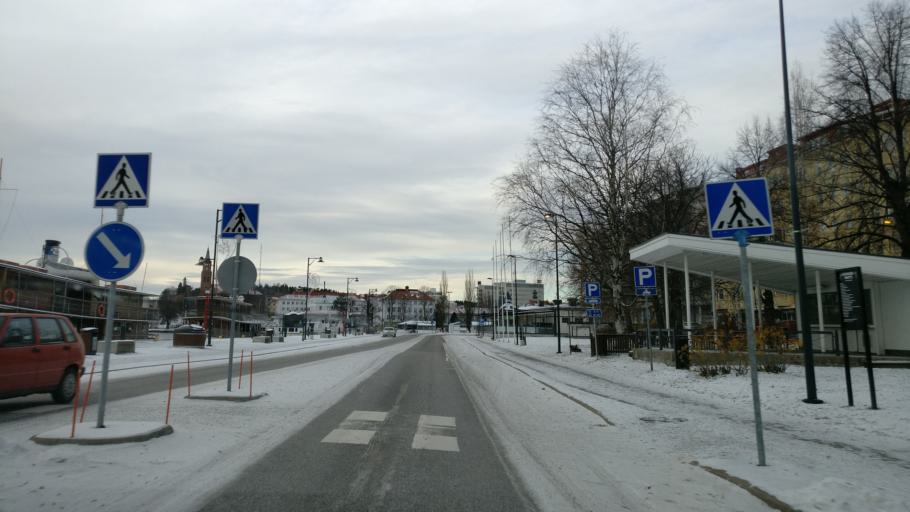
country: FI
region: Southern Savonia
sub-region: Savonlinna
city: Savonlinna
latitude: 61.8666
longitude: 28.8873
